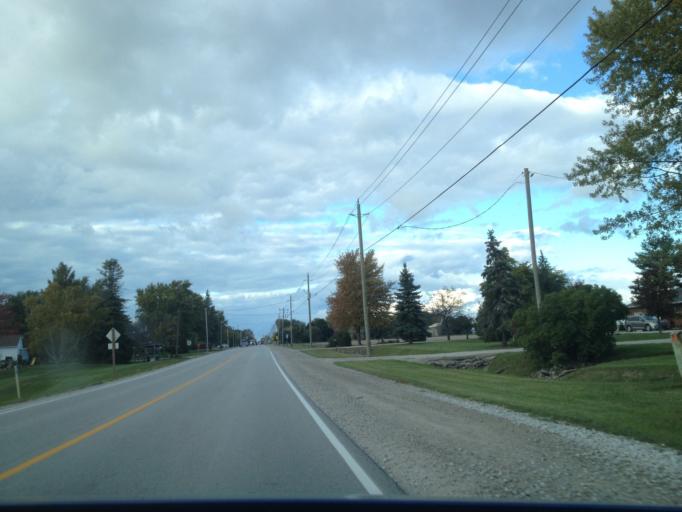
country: US
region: Michigan
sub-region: Wayne County
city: Grosse Pointe Farms
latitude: 42.2700
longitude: -82.7134
